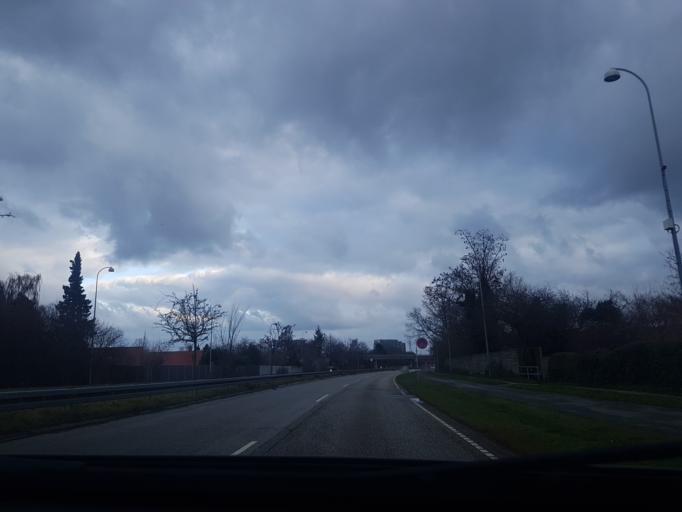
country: DK
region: Capital Region
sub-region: Vallensbaek Kommune
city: Vallensbaek
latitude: 55.6212
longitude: 12.3815
